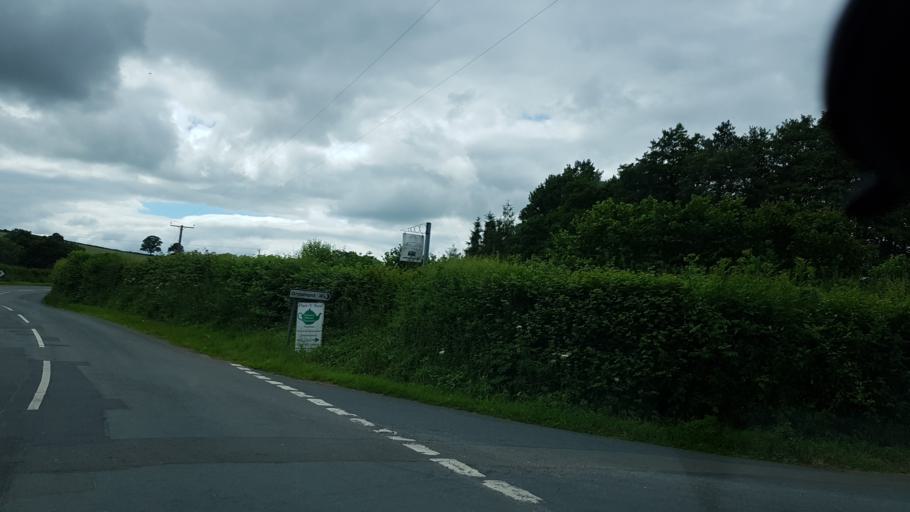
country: GB
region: England
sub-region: Herefordshire
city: Llanrothal
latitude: 51.8762
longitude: -2.8061
